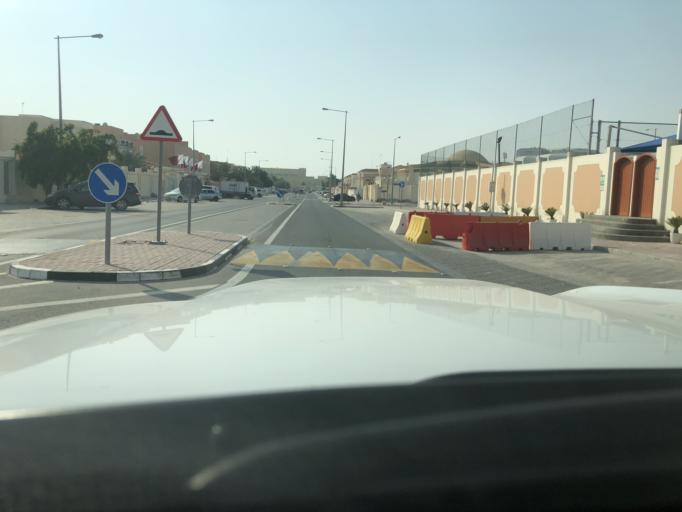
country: QA
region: Baladiyat ar Rayyan
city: Ar Rayyan
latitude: 25.3288
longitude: 51.4784
